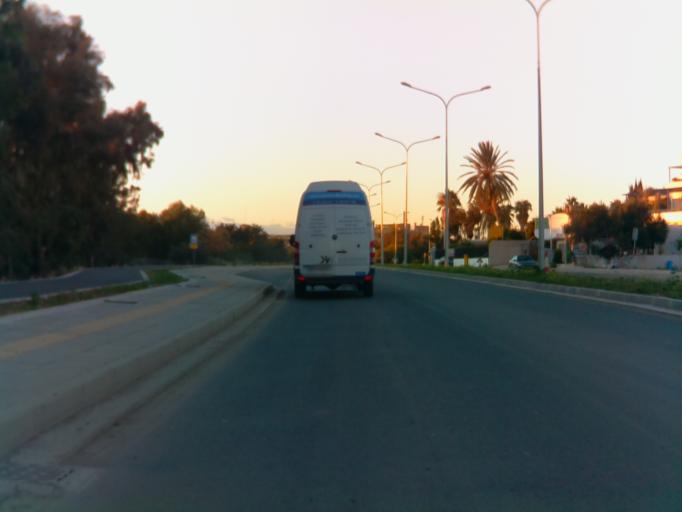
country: CY
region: Pafos
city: Paphos
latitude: 34.7761
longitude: 32.4078
